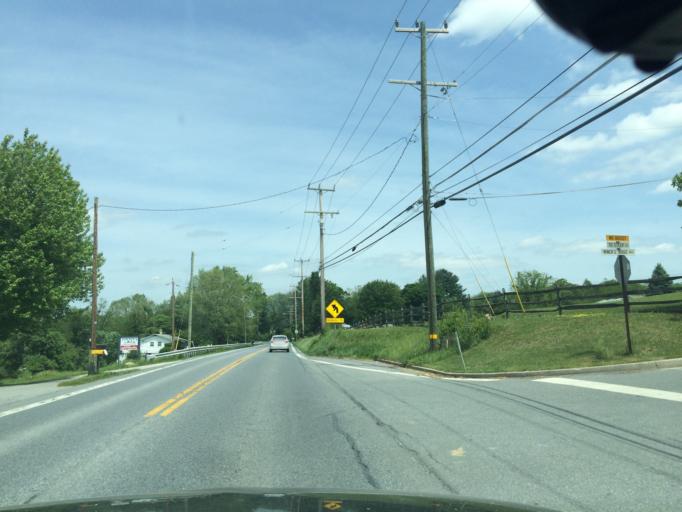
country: US
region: Maryland
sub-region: Carroll County
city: Eldersburg
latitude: 39.4422
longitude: -76.9325
